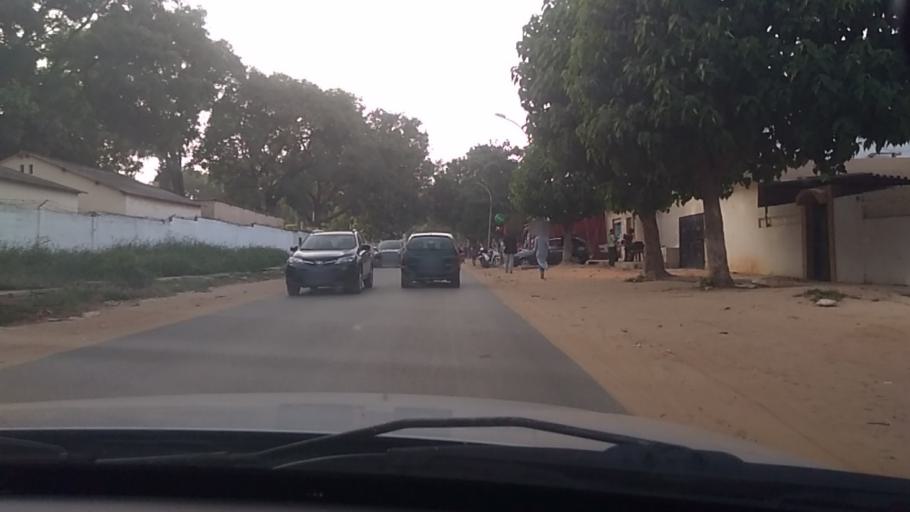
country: SN
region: Thies
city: Thies Nones
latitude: 14.7830
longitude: -16.9148
